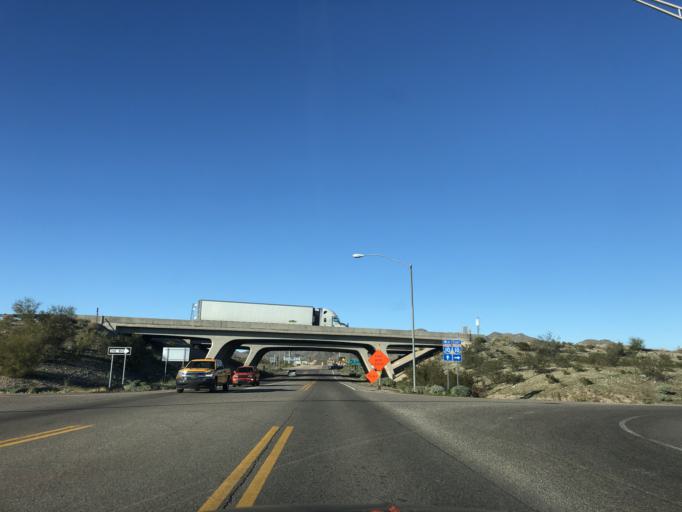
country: US
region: Arizona
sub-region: Maricopa County
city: Buckeye
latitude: 33.4326
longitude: -112.5909
